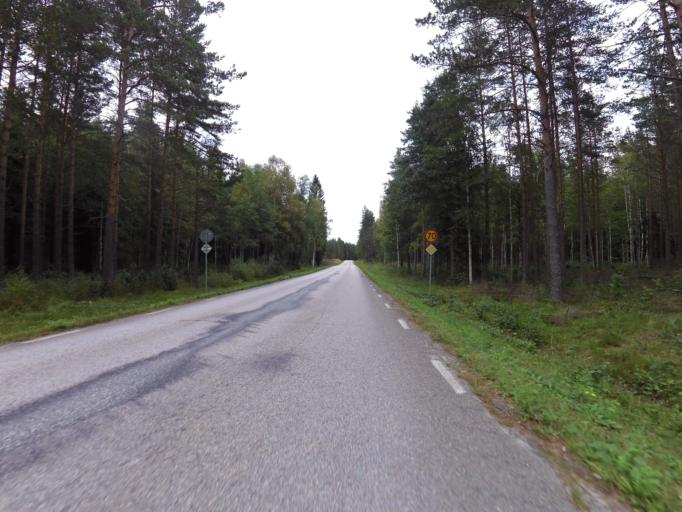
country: SE
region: Gaevleborg
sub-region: Sandvikens Kommun
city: Sandviken
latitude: 60.6629
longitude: 16.8689
